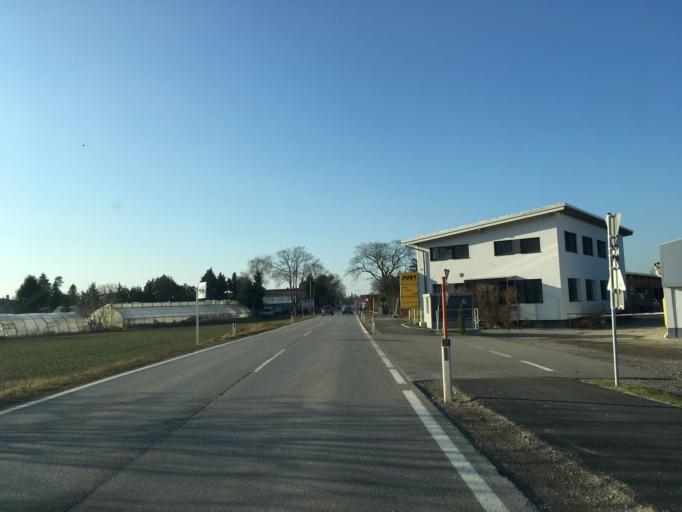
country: AT
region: Lower Austria
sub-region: Politischer Bezirk Tulln
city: Wordern
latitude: 48.3239
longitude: 16.1898
